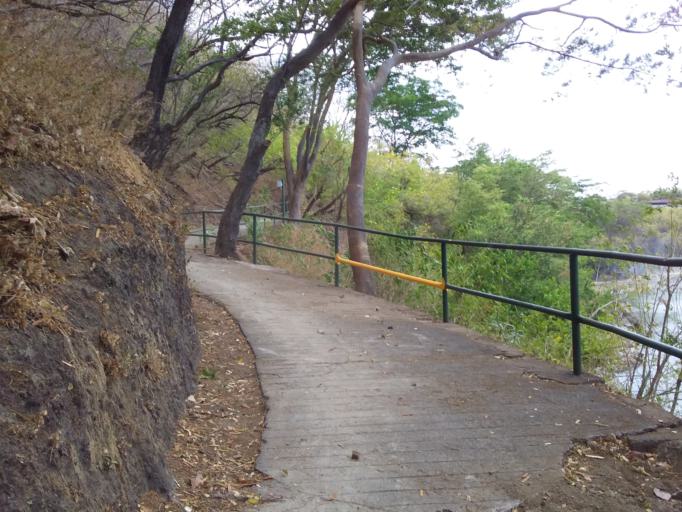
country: NI
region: Managua
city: Managua
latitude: 12.1415
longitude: -86.2707
